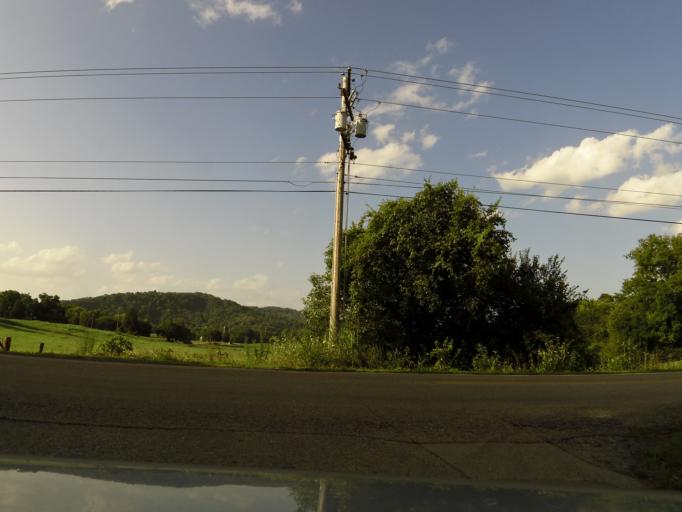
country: US
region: Tennessee
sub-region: Blount County
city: Eagleton Village
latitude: 35.8105
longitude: -83.9333
